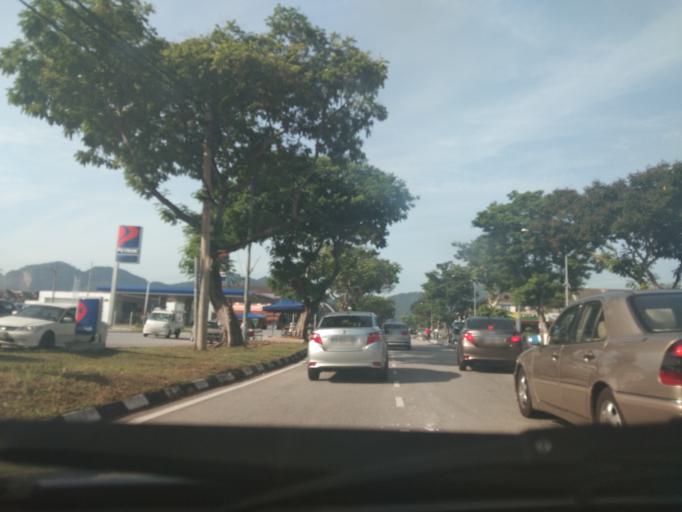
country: MY
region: Perak
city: Ipoh
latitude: 4.5805
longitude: 101.1273
